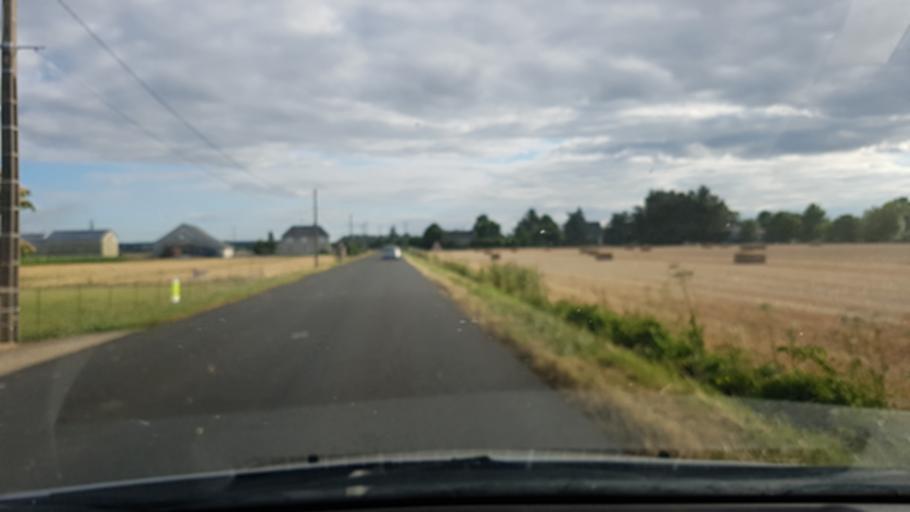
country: FR
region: Pays de la Loire
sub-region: Departement de Maine-et-Loire
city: Saint-Mathurin-sur-Loire
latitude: 47.4326
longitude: -0.2972
